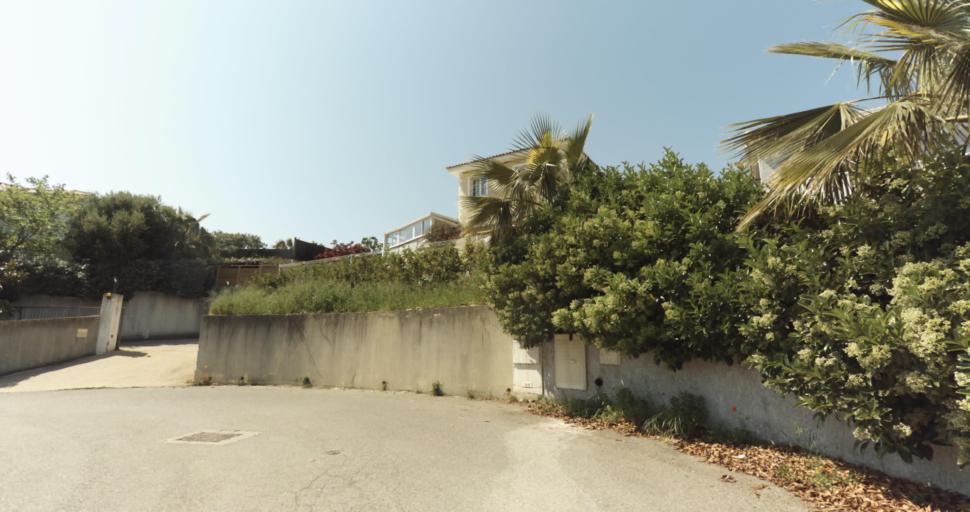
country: FR
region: Corsica
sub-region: Departement de la Haute-Corse
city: Biguglia
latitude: 42.6141
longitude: 9.4274
